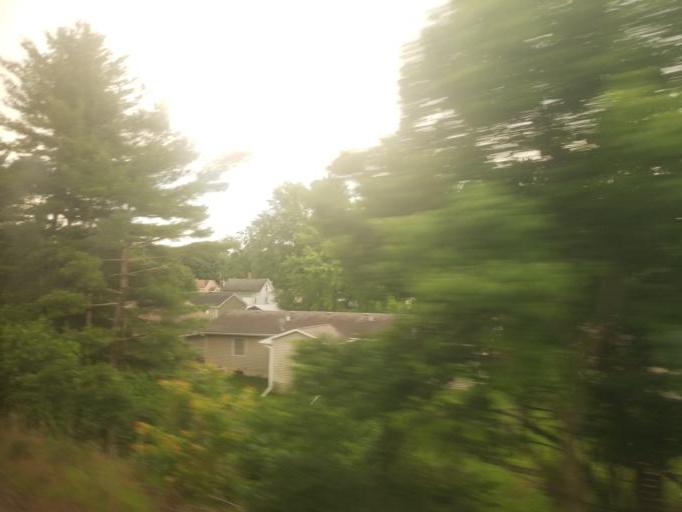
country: US
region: Illinois
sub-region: Bureau County
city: Princeton
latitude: 41.3855
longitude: -89.4720
